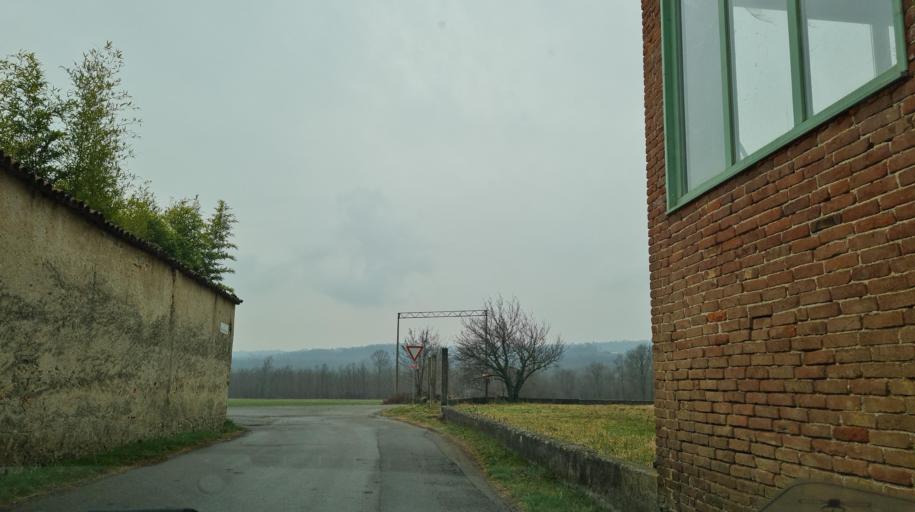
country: IT
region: Piedmont
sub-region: Provincia di Biella
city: Borriana
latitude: 45.5115
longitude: 8.0275
